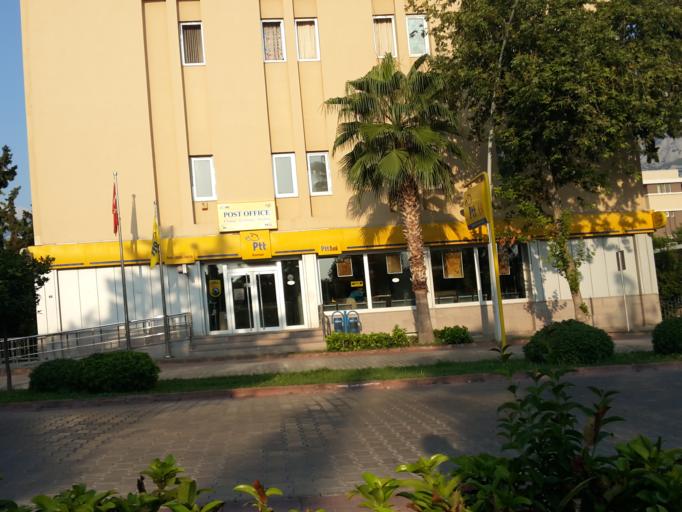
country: TR
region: Antalya
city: Kemer
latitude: 36.6034
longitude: 30.5596
